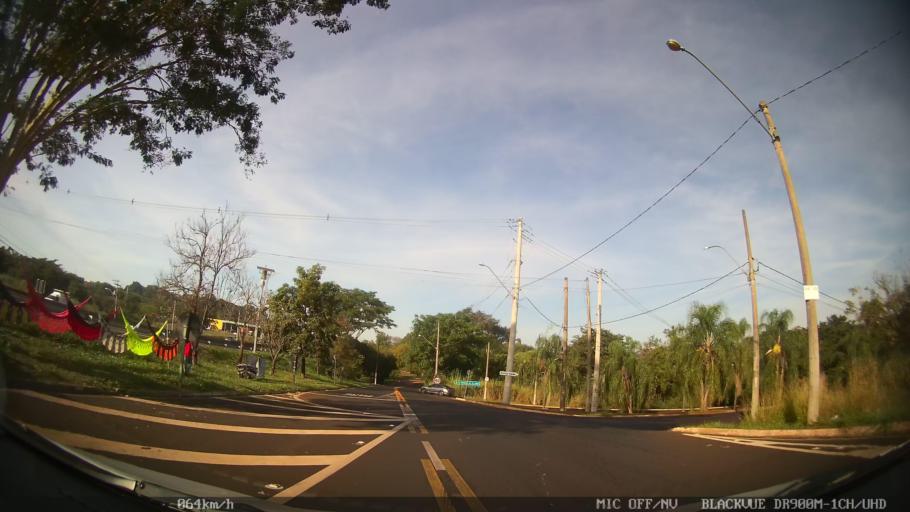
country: BR
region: Sao Paulo
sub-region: Ribeirao Preto
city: Ribeirao Preto
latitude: -21.2471
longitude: -47.8197
